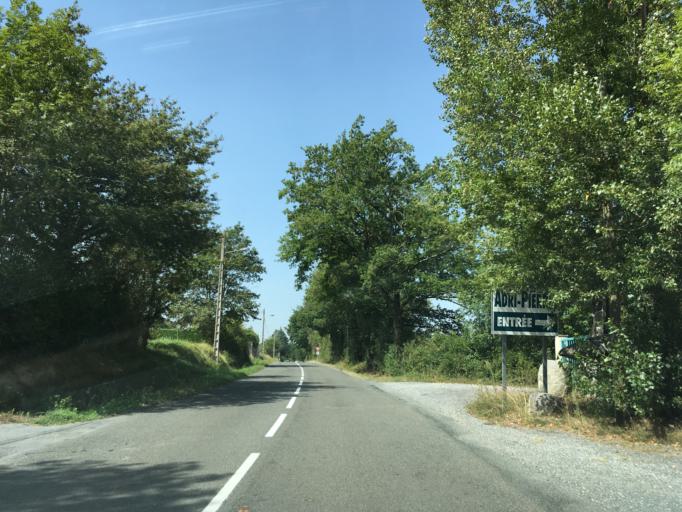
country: FR
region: Midi-Pyrenees
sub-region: Departement du Tarn
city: Burlats
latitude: 43.6203
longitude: 2.2905
